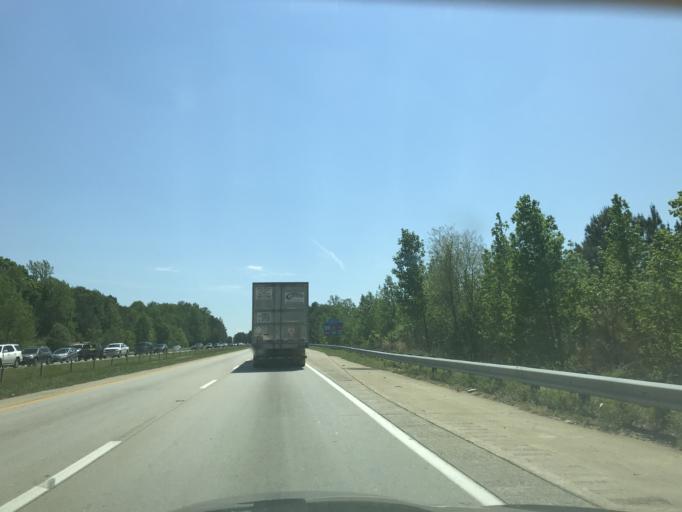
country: US
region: North Carolina
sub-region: Wake County
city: Garner
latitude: 35.6209
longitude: -78.5673
